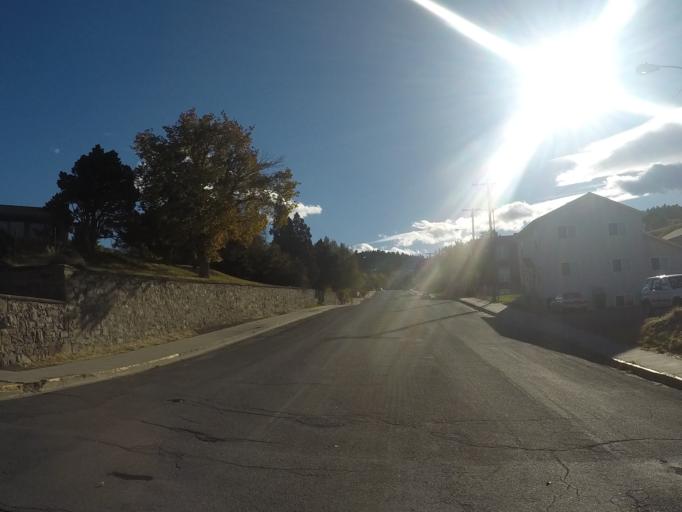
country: US
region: Montana
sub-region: Lewis and Clark County
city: Helena
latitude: 46.5829
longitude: -112.0372
